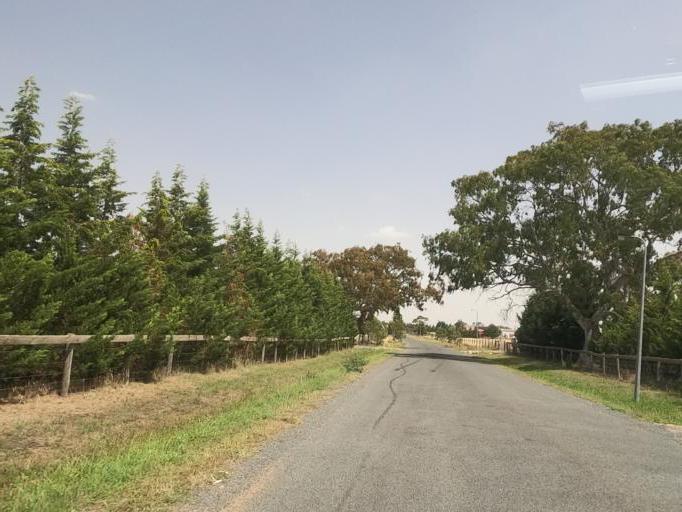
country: AU
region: Victoria
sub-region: Hume
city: Craigieburn
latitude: -37.5582
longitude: 144.8978
